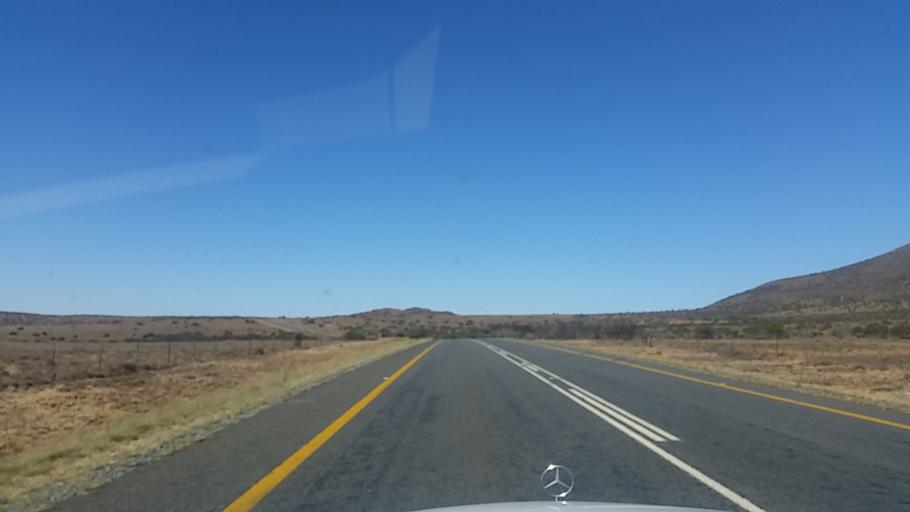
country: ZA
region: Eastern Cape
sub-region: Cacadu District Municipality
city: Graaff-Reinet
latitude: -32.0377
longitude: 24.6210
